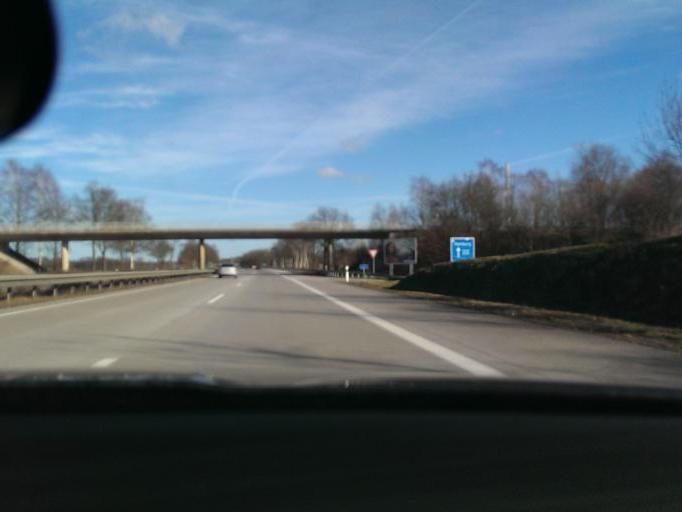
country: DE
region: Lower Saxony
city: Langenhagen
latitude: 52.5114
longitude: 9.7687
